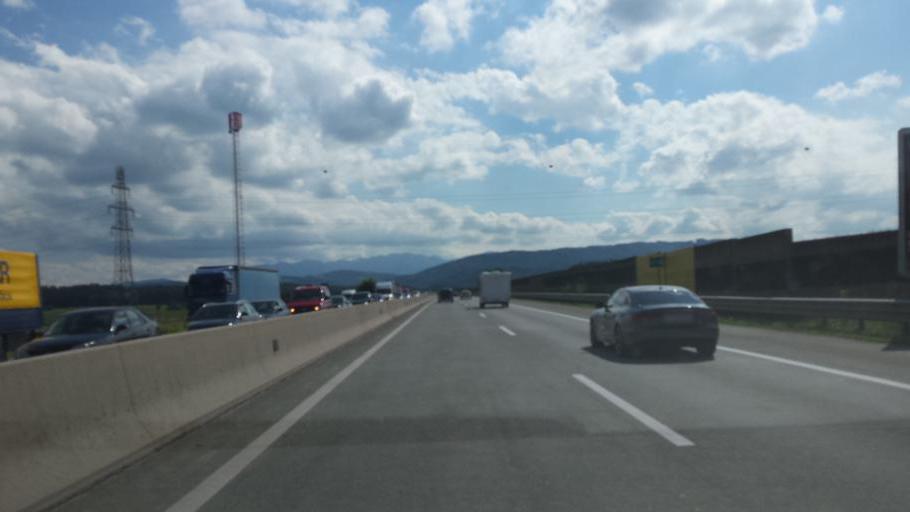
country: AT
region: Upper Austria
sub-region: Politischer Bezirk Vocklabruck
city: Desselbrunn
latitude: 47.9817
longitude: 13.7742
